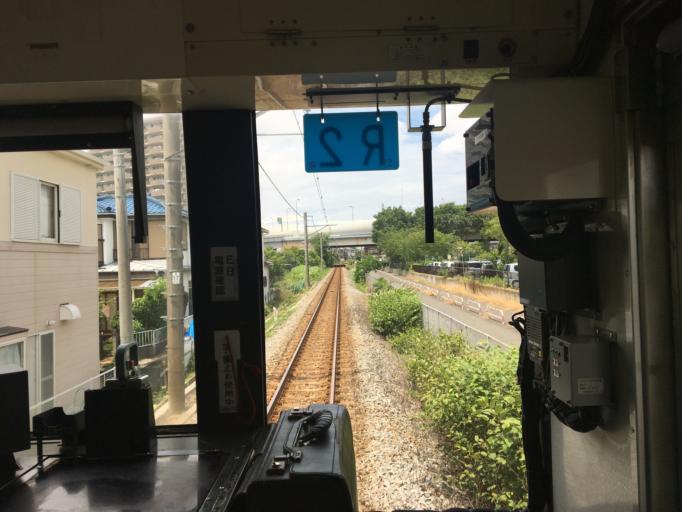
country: JP
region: Kanagawa
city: Chigasaki
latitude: 35.3490
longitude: 139.4023
